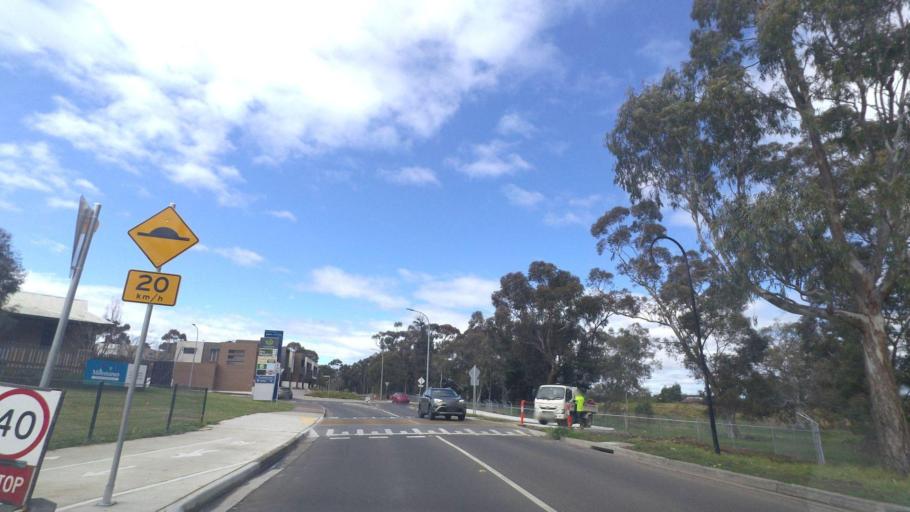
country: AU
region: Victoria
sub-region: Darebin
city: Kingsbury
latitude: -37.7138
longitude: 145.0470
